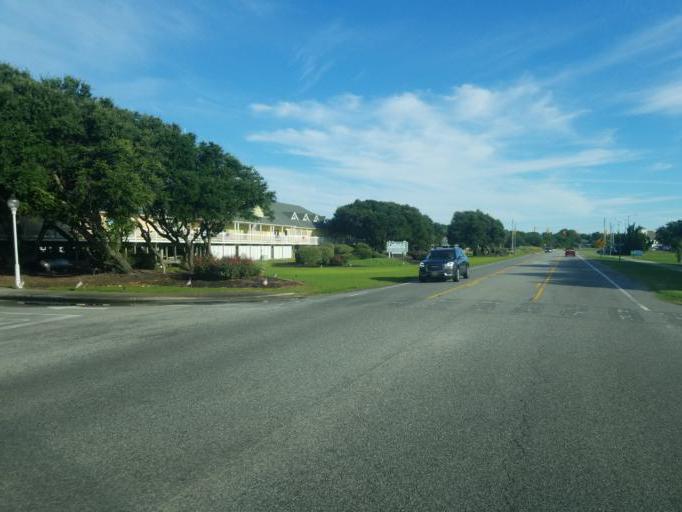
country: US
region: North Carolina
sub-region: Dare County
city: Southern Shores
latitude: 36.3254
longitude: -75.8172
